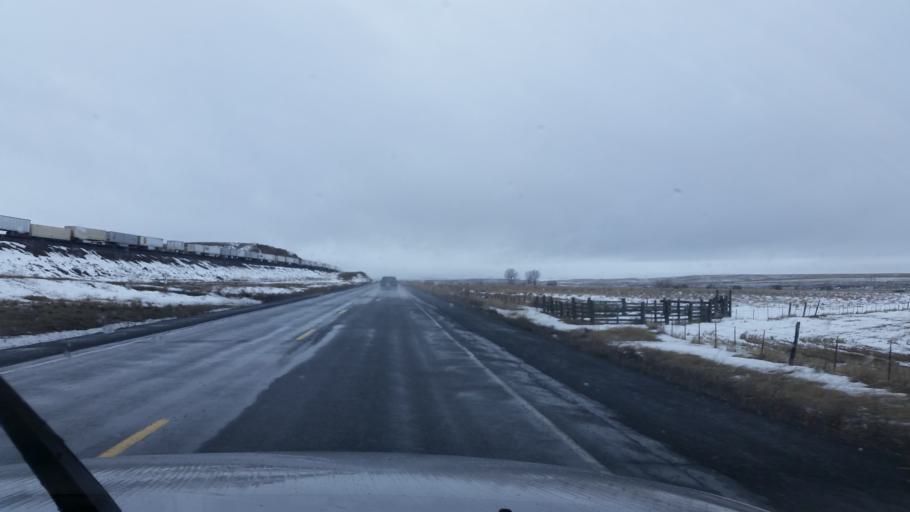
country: US
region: Washington
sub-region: Lincoln County
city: Davenport
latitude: 47.5004
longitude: -118.2352
